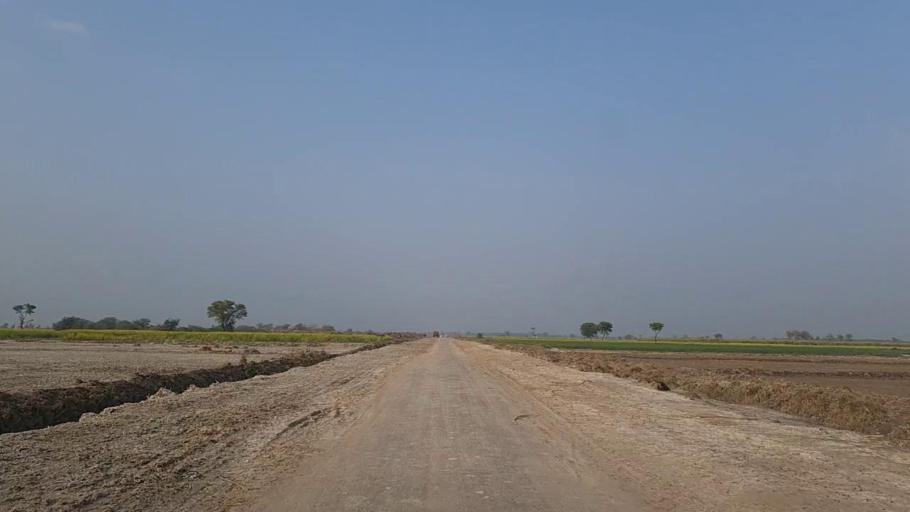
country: PK
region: Sindh
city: Jam Sahib
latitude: 26.3312
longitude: 68.5146
